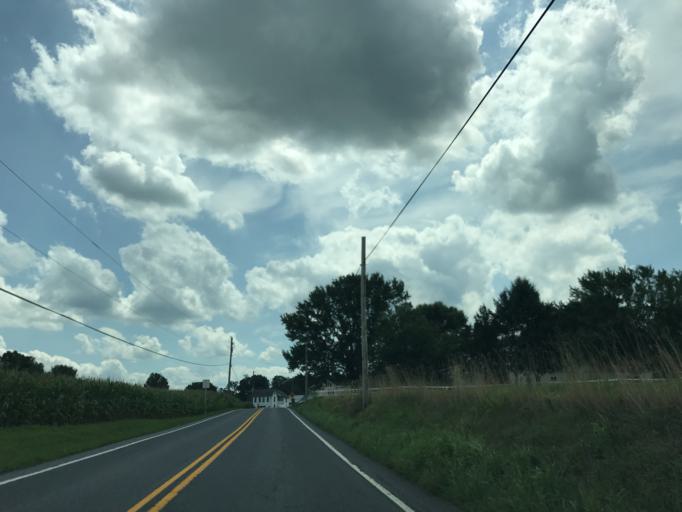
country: US
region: Pennsylvania
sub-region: Lancaster County
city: Manheim
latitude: 40.1927
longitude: -76.4532
